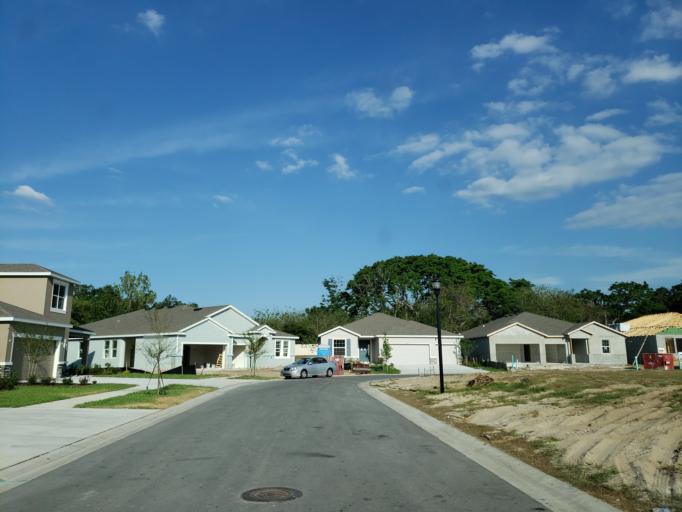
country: US
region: Florida
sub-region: Hillsborough County
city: Brandon
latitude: 27.9123
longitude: -82.2825
